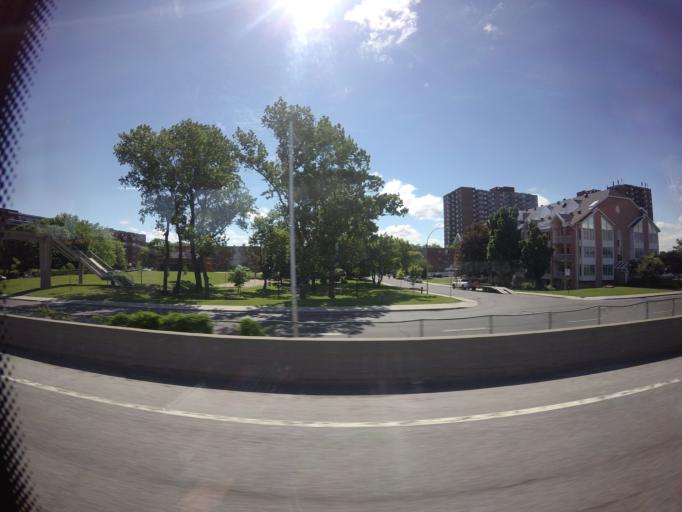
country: CA
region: Quebec
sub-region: Monteregie
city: Longueuil
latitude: 45.5336
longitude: -73.5189
